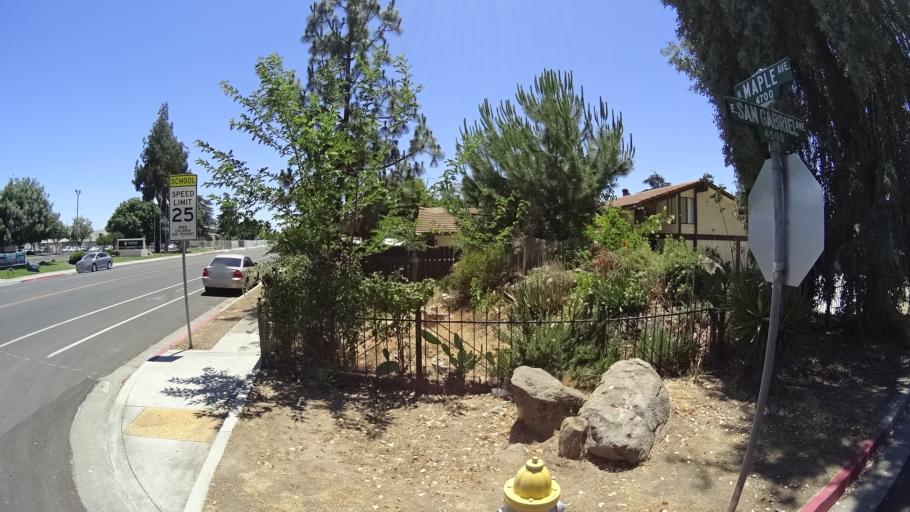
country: US
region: California
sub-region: Fresno County
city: Tarpey Village
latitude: 36.8040
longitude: -119.7454
